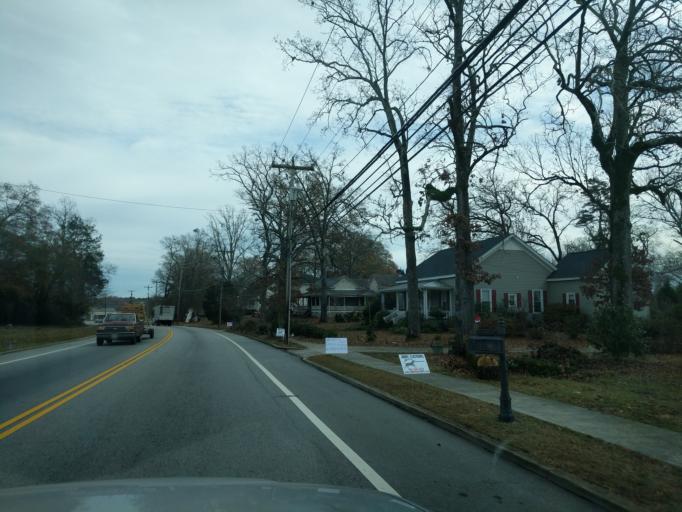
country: US
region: South Carolina
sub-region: Anderson County
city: Williamston
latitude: 34.6435
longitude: -82.4650
